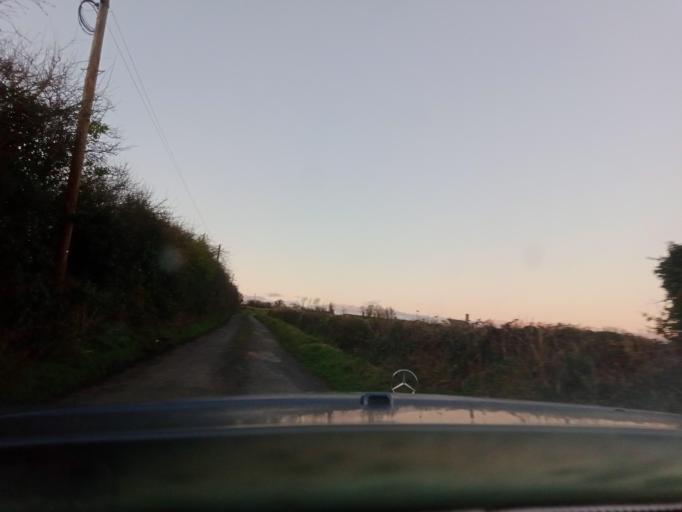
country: IE
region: Leinster
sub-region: Kilkenny
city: Graiguenamanagh
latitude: 52.5734
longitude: -6.9593
